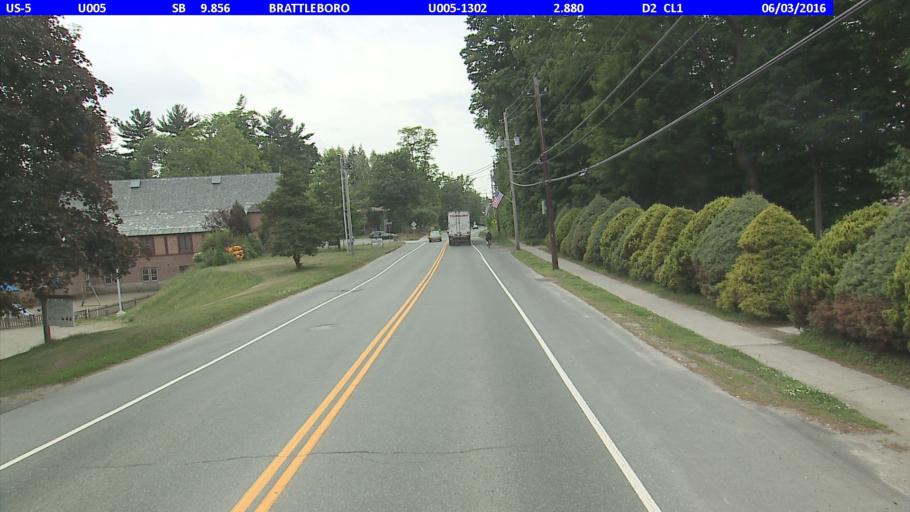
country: US
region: Vermont
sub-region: Windham County
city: Brattleboro
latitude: 42.8605
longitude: -72.5580
